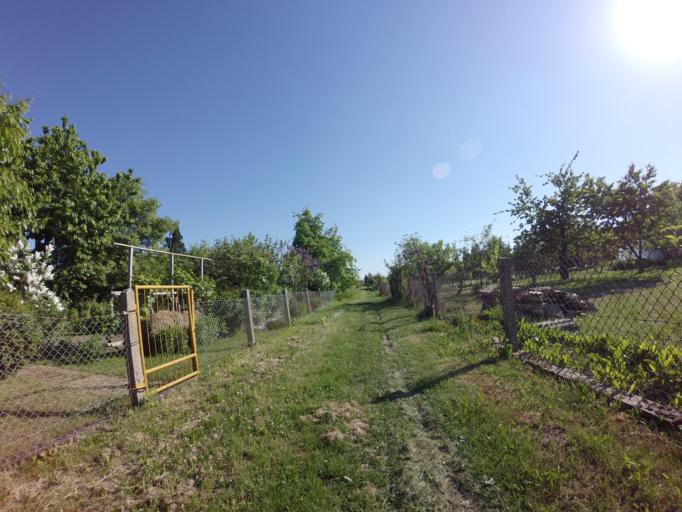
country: PL
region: West Pomeranian Voivodeship
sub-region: Powiat choszczenski
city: Choszczno
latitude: 53.1576
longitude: 15.3990
